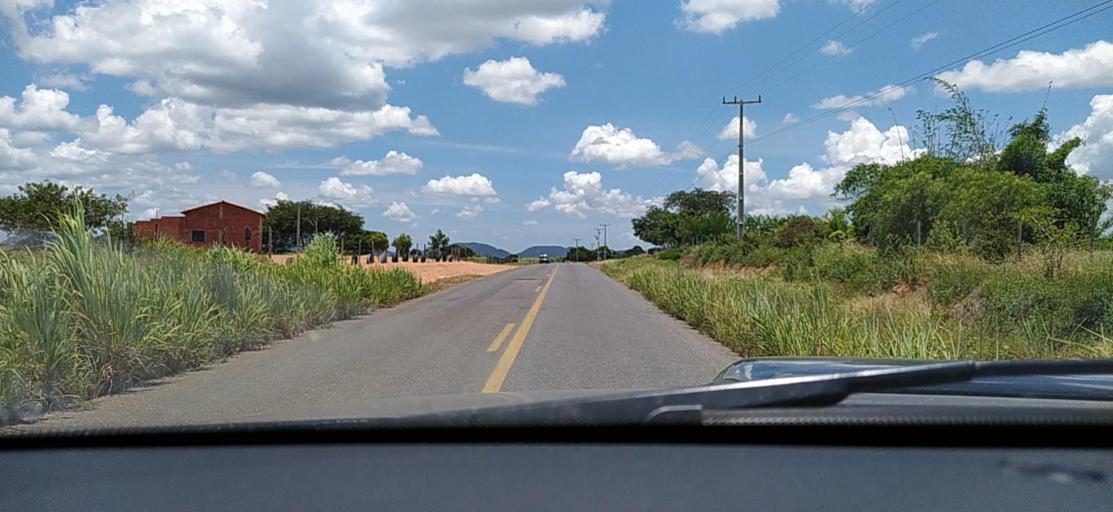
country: BR
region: Bahia
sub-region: Guanambi
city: Guanambi
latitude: -14.1055
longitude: -42.8675
